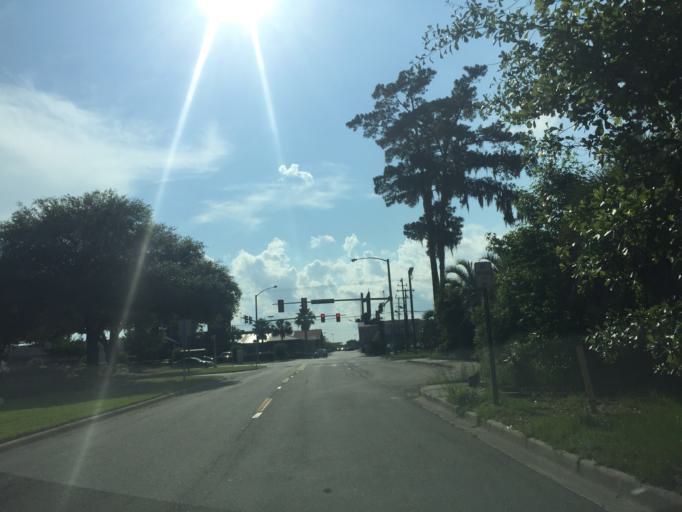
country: US
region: Georgia
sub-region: Chatham County
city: Isle of Hope
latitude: 32.0051
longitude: -81.1097
